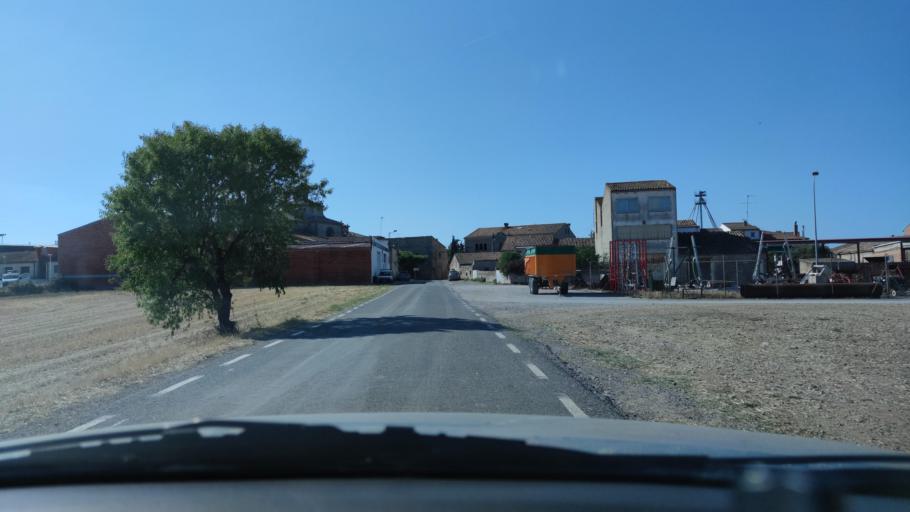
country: ES
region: Catalonia
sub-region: Provincia de Lleida
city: Ivorra
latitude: 41.7273
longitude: 1.3675
